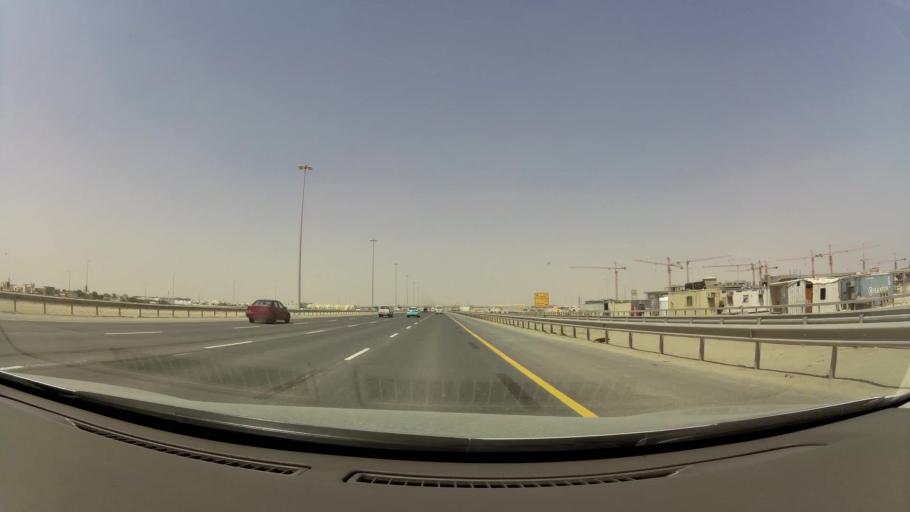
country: QA
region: Baladiyat Umm Salal
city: Umm Salal Muhammad
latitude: 25.4031
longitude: 51.4288
